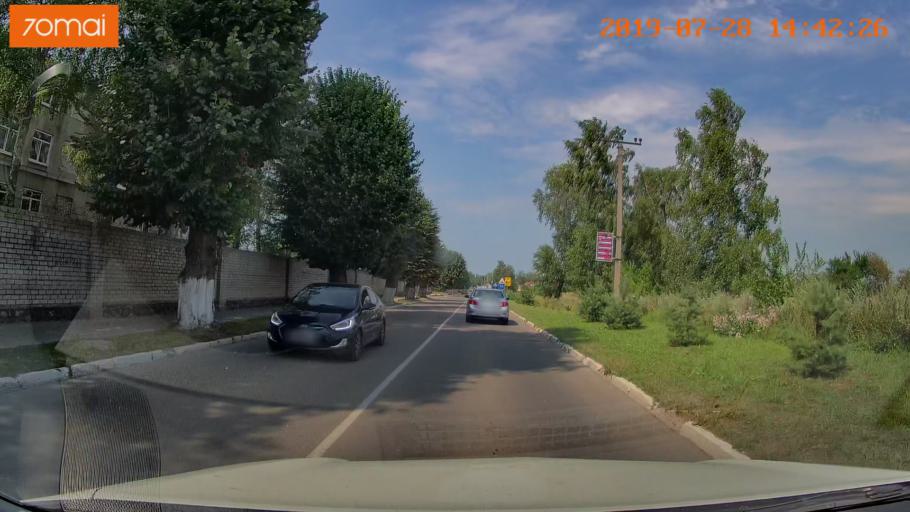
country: RU
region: Kaliningrad
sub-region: Gorod Kaliningrad
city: Yantarnyy
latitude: 54.8599
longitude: 19.9421
